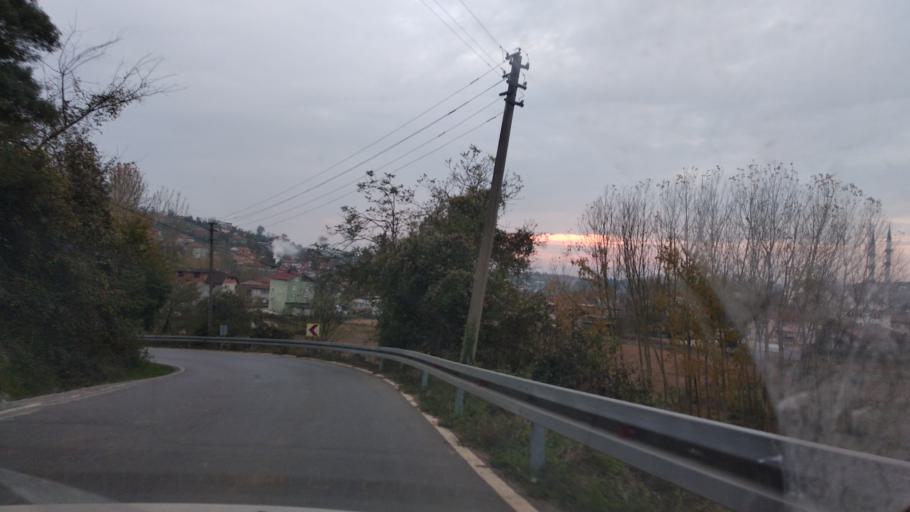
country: TR
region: Sakarya
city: Ortakoy
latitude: 41.0384
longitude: 30.6474
